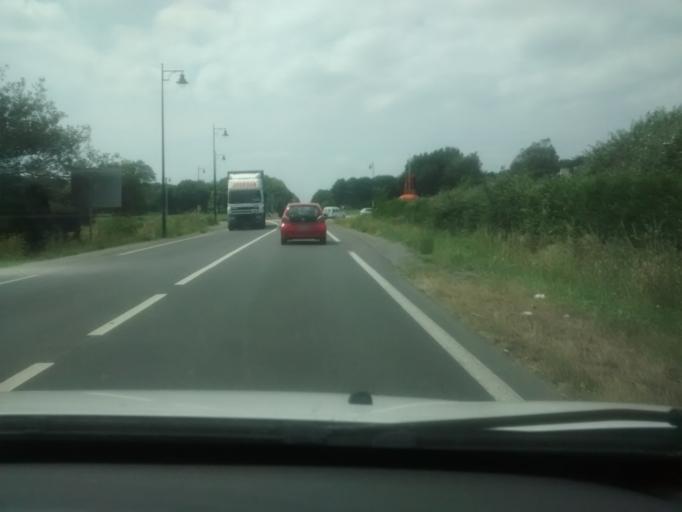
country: FR
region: Brittany
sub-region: Departement d'Ille-et-Vilaine
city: Dinard
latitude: 48.6114
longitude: -2.0705
